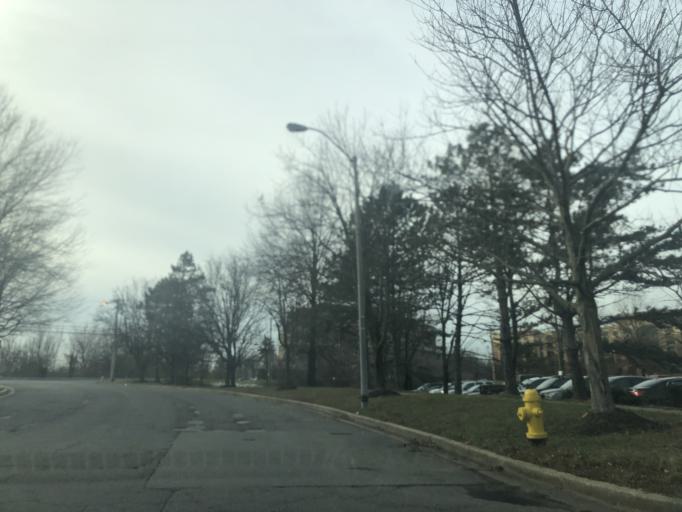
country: US
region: Maryland
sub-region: Howard County
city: Elkridge
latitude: 39.2060
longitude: -76.6906
